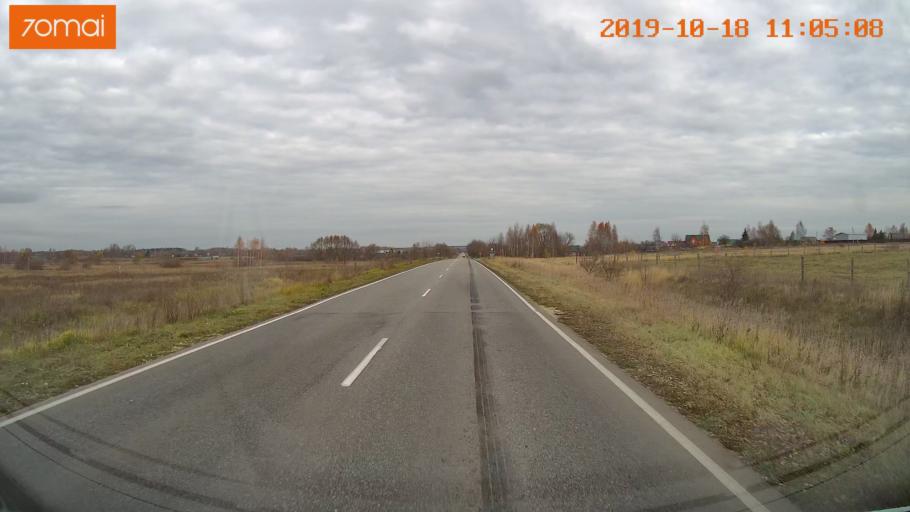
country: RU
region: Tula
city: Kimovsk
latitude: 53.9021
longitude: 38.5417
